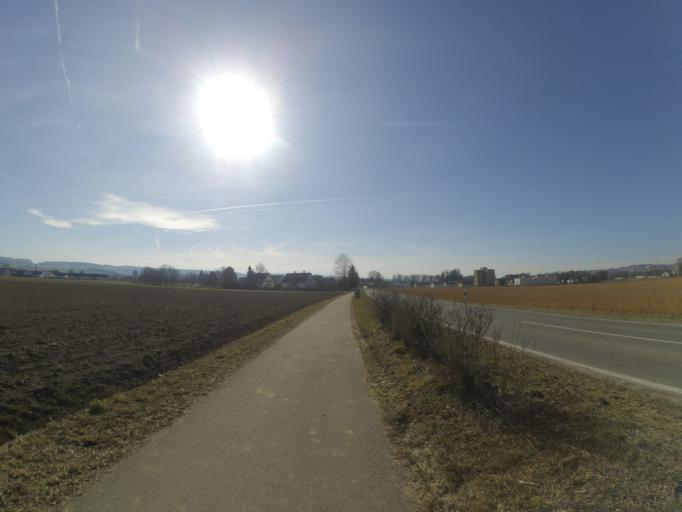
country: DE
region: Baden-Wuerttemberg
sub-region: Tuebingen Region
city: Baienfurt
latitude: 47.8330
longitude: 9.6383
